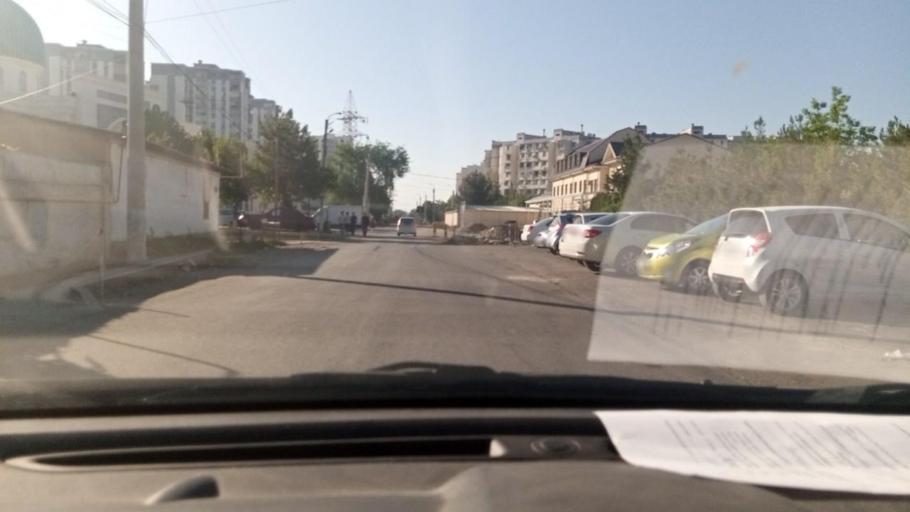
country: UZ
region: Toshkent
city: Salor
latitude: 41.3239
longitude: 69.3568
